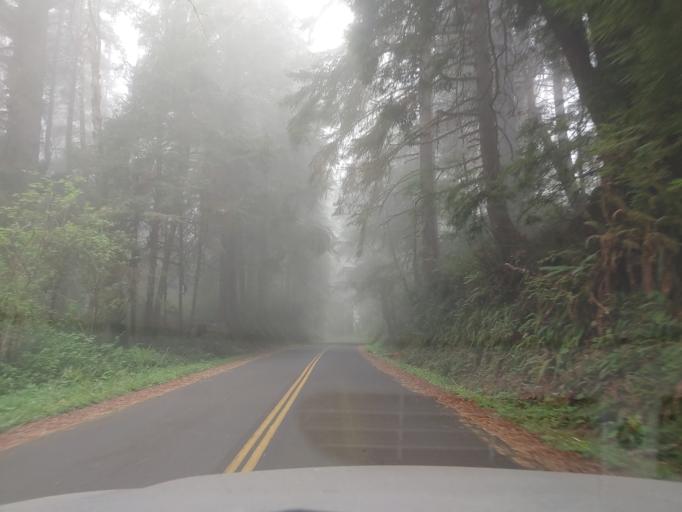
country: US
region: California
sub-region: Del Norte County
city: Bertsch-Oceanview
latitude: 41.4584
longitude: -124.0497
